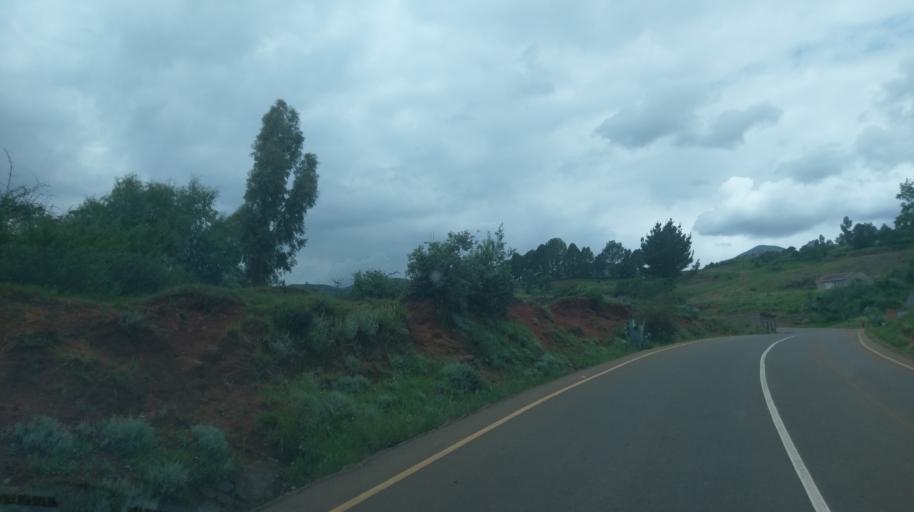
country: LS
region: Butha-Buthe
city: Butha-Buthe
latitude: -29.0358
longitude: 28.2819
